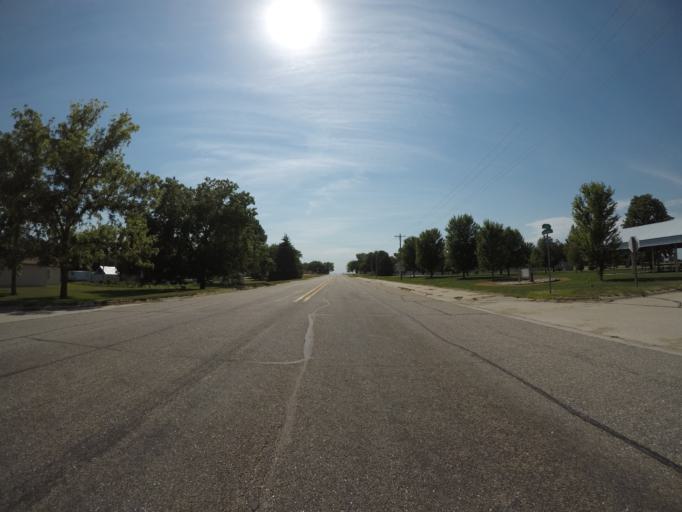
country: US
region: Nebraska
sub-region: Adams County
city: Hastings
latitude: 40.4663
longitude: -98.6534
